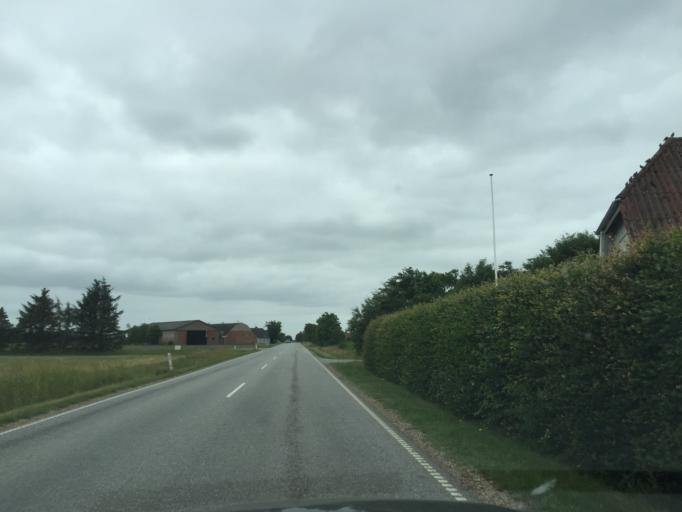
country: DK
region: South Denmark
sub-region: Esbjerg Kommune
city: Ribe
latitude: 55.3688
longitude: 8.8077
